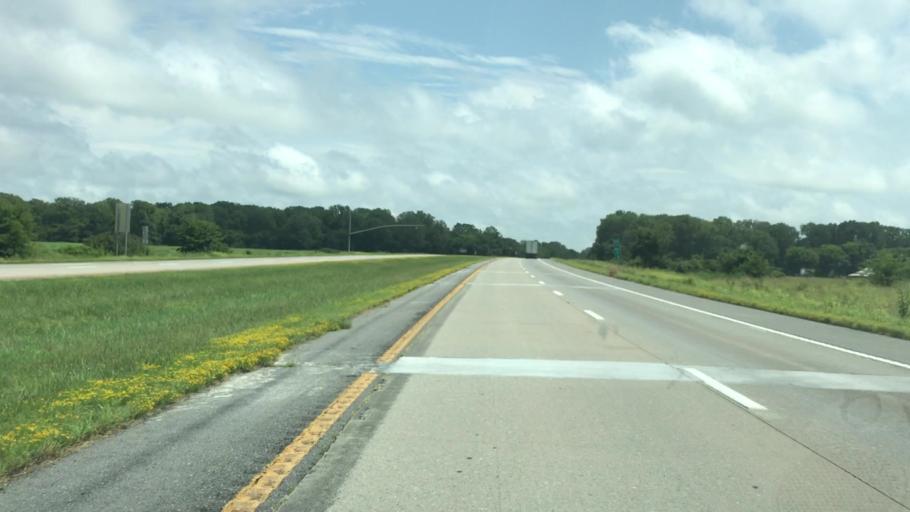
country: US
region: Missouri
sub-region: Pemiscot County
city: Caruthersville
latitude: 36.1379
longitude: -89.6329
